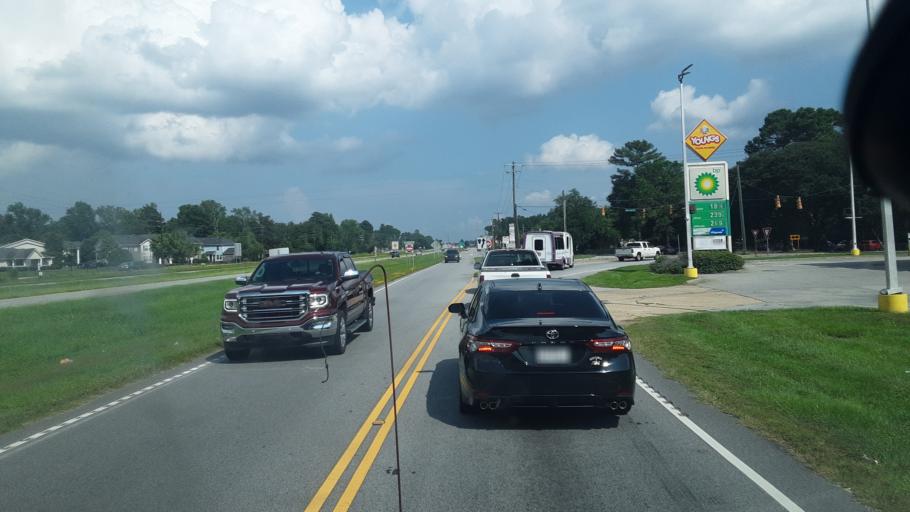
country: US
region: South Carolina
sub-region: Sumter County
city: Sumter
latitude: 33.9470
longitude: -80.3547
